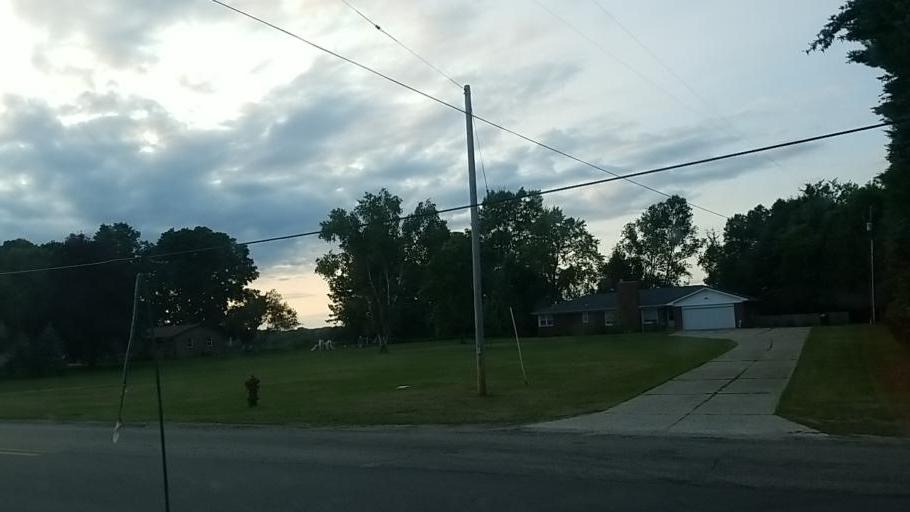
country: US
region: Michigan
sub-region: Newaygo County
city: Newaygo
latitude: 43.4165
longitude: -85.7870
